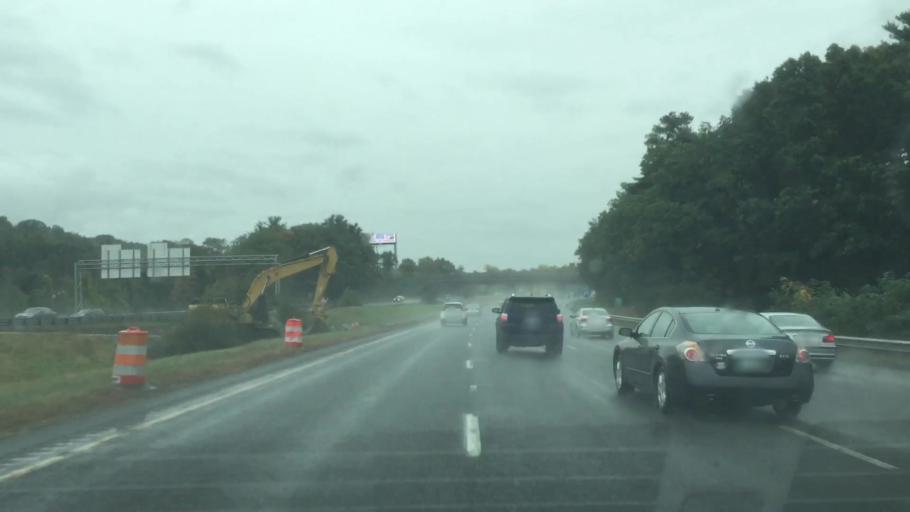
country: US
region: Massachusetts
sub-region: Essex County
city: Lawrence
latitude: 42.7397
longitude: -71.1406
